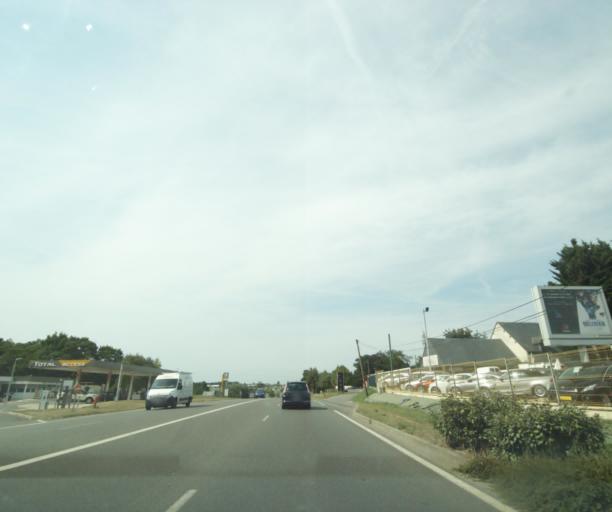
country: FR
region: Centre
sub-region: Departement d'Indre-et-Loire
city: Chambray-les-Tours
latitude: 47.3158
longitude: 0.7113
